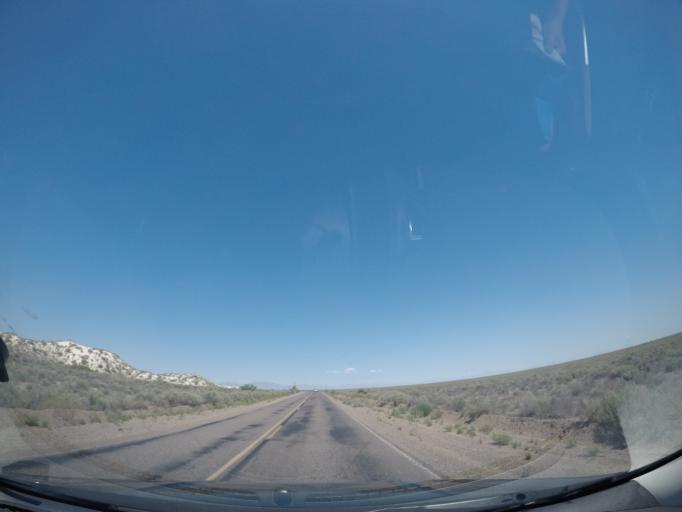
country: US
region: New Mexico
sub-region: Otero County
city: Holloman Air Force Base
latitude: 32.7858
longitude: -106.1815
